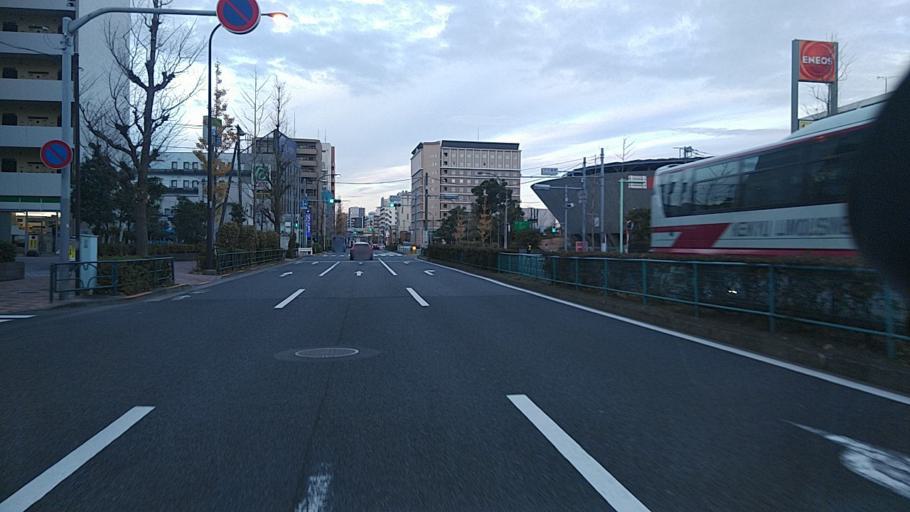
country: JP
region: Kanagawa
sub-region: Kawasaki-shi
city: Kawasaki
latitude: 35.5509
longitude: 139.7510
